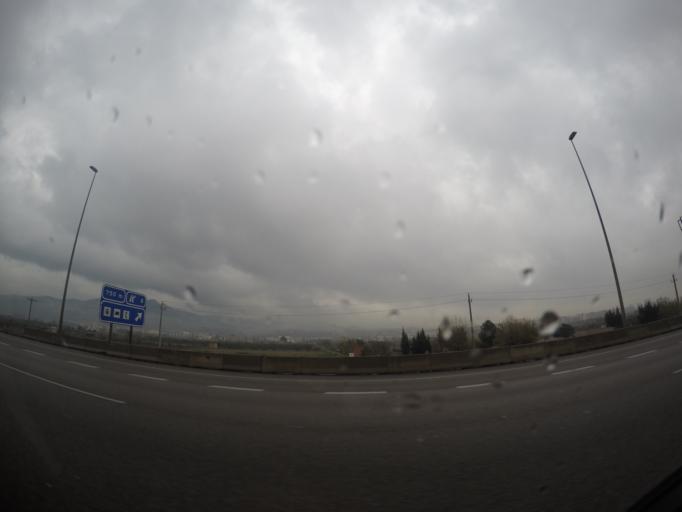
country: ES
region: Catalonia
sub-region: Provincia de Barcelona
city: Sant Feliu de Llobregat
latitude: 41.3833
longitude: 2.0289
